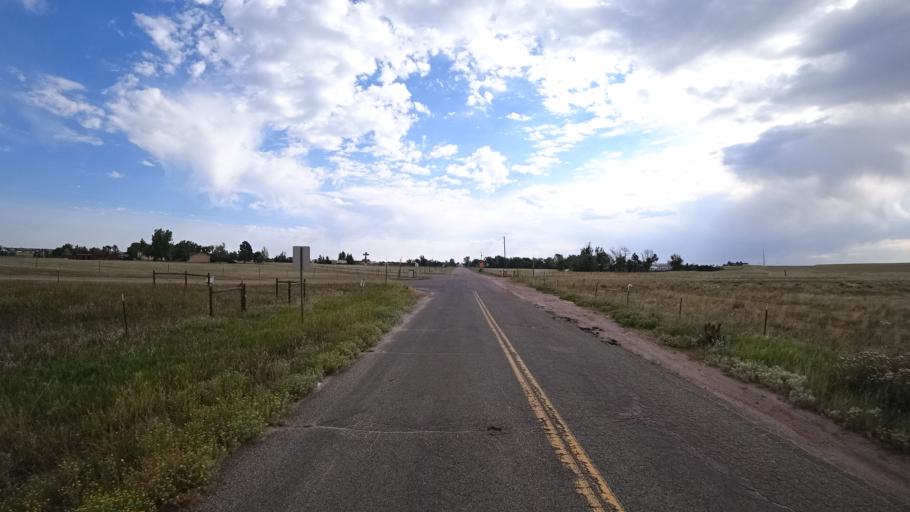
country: US
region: Colorado
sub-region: El Paso County
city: Cimarron Hills
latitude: 38.9116
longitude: -104.6739
